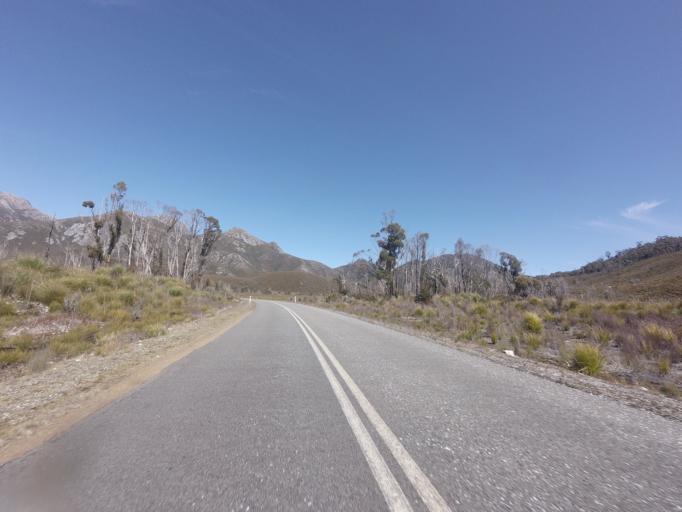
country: AU
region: Tasmania
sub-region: Huon Valley
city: Geeveston
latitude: -42.8579
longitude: 146.1928
